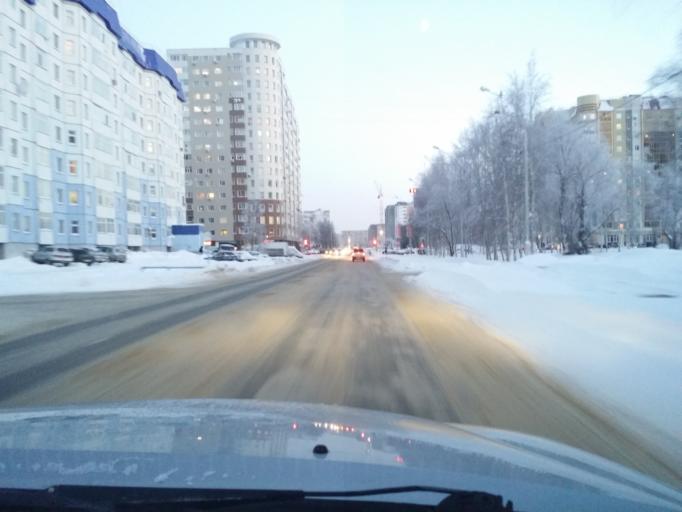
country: RU
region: Khanty-Mansiyskiy Avtonomnyy Okrug
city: Nizhnevartovsk
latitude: 60.9354
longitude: 76.5766
